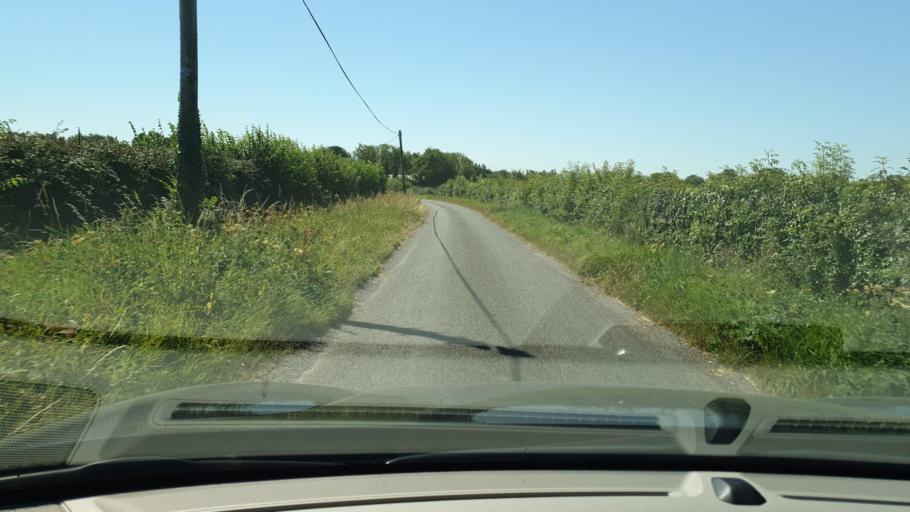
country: IE
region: Leinster
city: Hartstown
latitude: 53.4400
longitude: -6.4302
